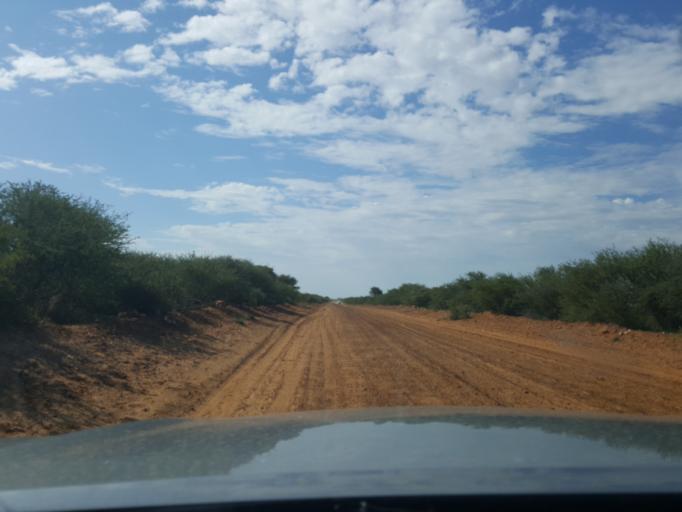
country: BW
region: Kweneng
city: Khudumelapye
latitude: -23.6248
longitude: 24.7274
